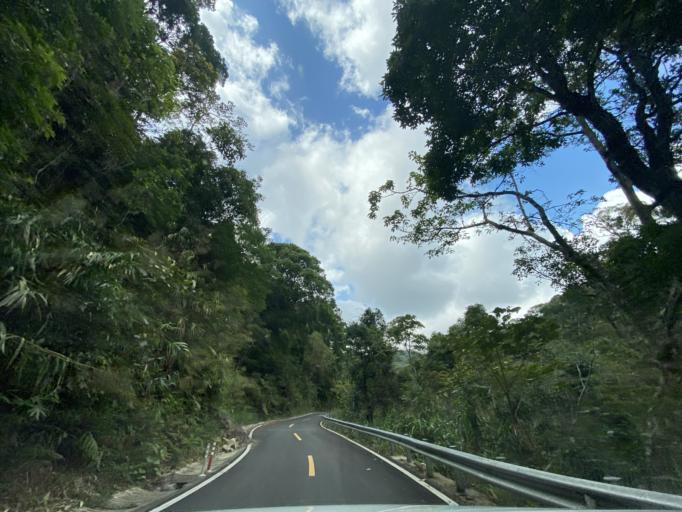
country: CN
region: Hainan
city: Benhao
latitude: 18.6943
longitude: 109.8805
